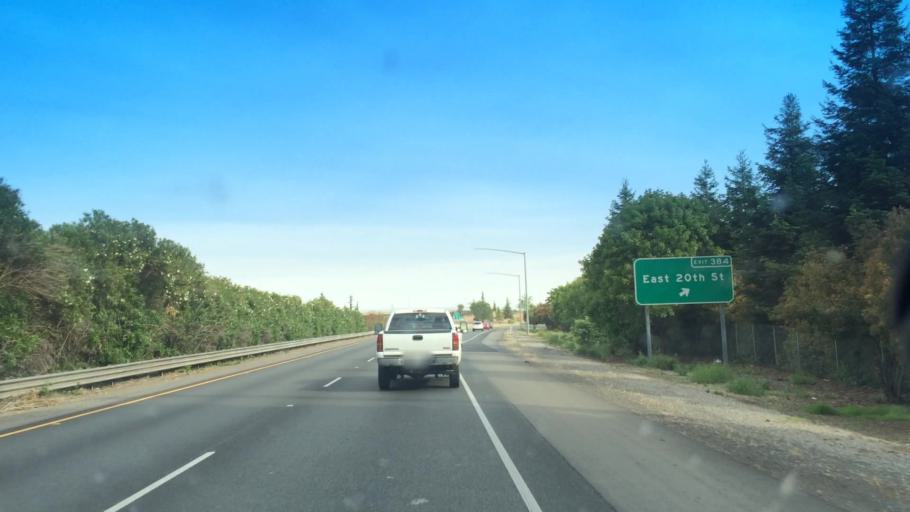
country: US
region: California
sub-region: Butte County
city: Chico
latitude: 39.7298
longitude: -121.8123
